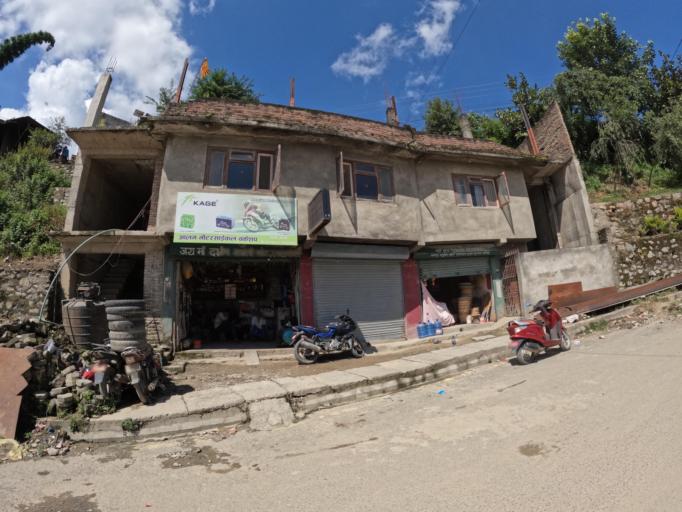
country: NP
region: Central Region
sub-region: Bagmati Zone
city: Kathmandu
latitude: 27.7446
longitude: 85.3293
